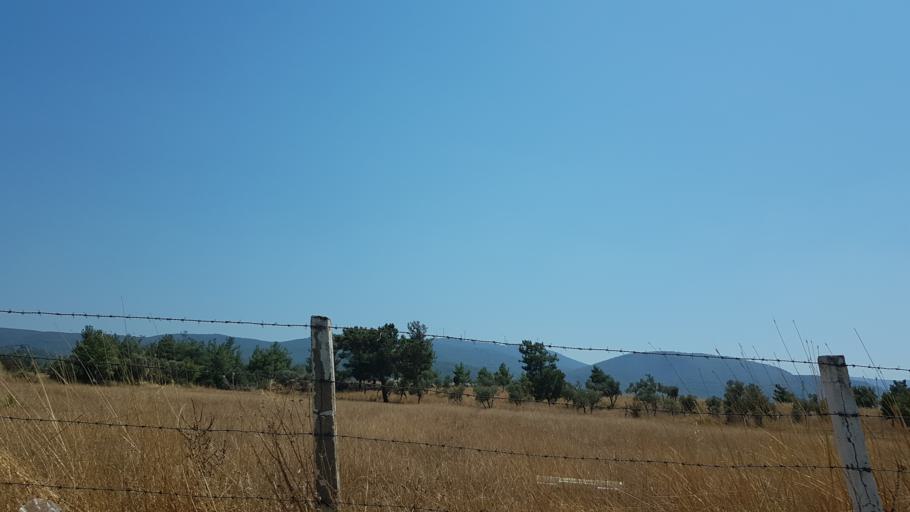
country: TR
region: Mugla
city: Karaova
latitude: 37.1047
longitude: 27.6554
